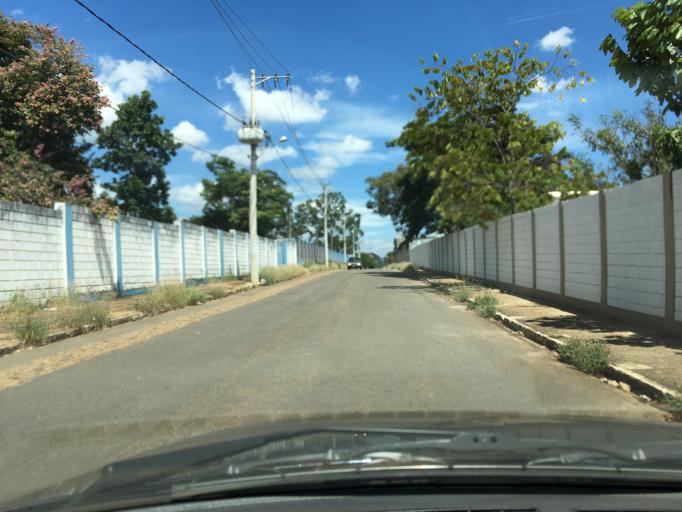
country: BR
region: Minas Gerais
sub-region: Mateus Leme
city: Mateus Leme
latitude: -19.9964
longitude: -44.4372
